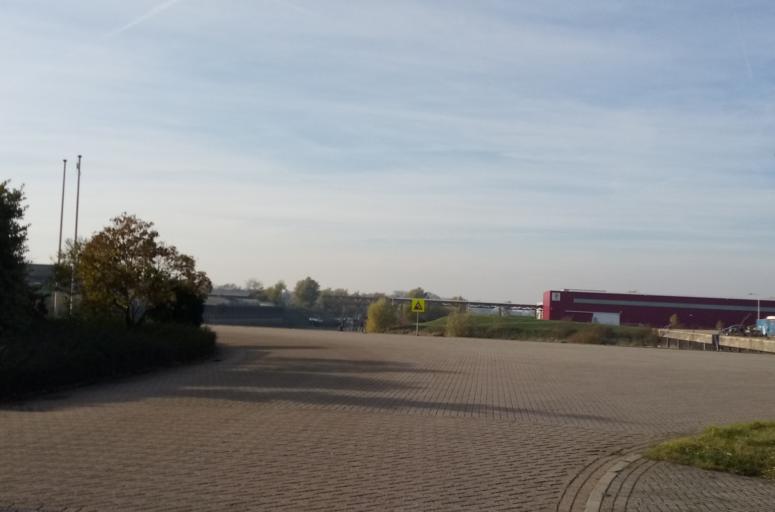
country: NL
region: Gelderland
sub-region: Gemeente Zutphen
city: Zutphen
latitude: 52.1562
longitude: 6.1960
